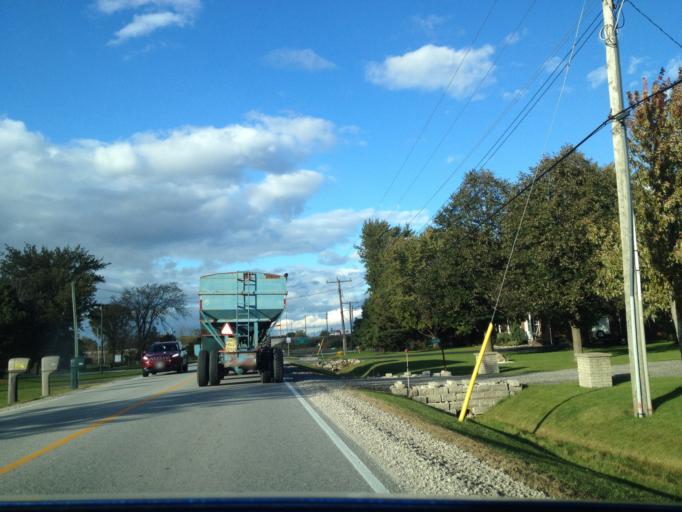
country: US
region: Michigan
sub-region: Wayne County
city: Grosse Pointe
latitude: 42.2337
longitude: -82.7131
